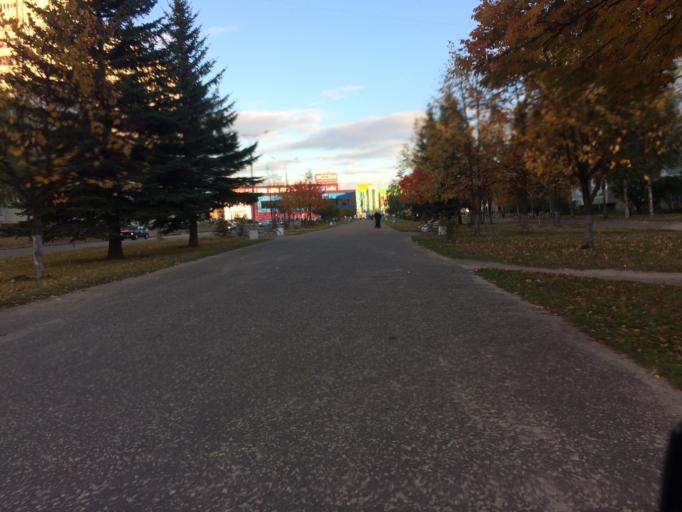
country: RU
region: Mariy-El
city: Yoshkar-Ola
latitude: 56.6294
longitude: 47.9240
